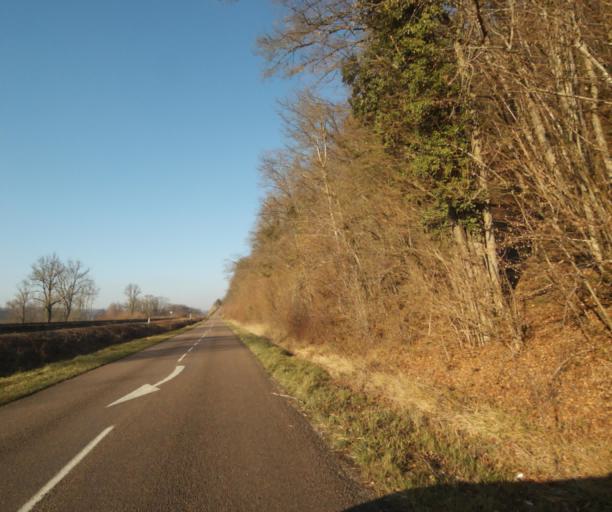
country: FR
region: Champagne-Ardenne
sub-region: Departement de la Haute-Marne
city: Chevillon
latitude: 48.5109
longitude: 5.1216
